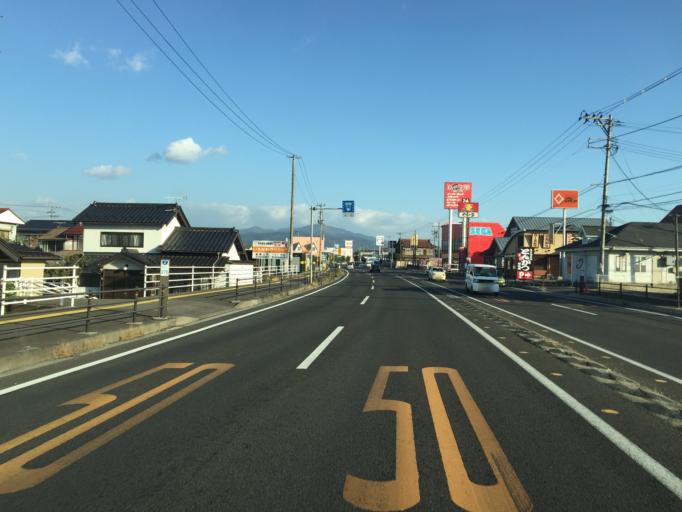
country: JP
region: Fukushima
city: Fukushima-shi
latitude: 37.7838
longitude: 140.4871
